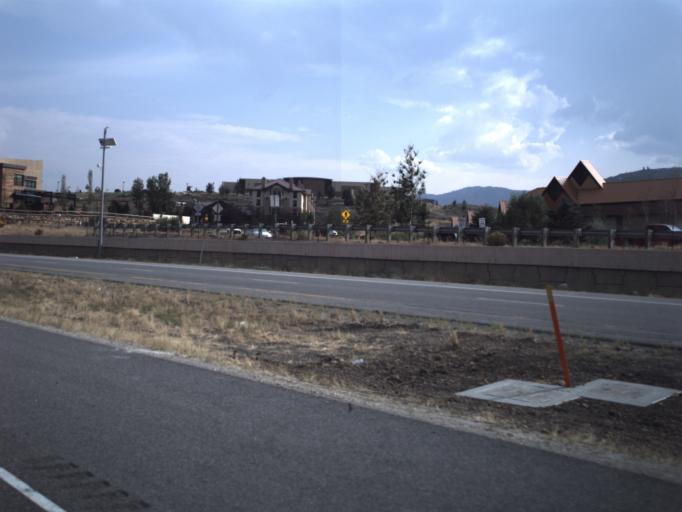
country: US
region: Utah
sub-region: Summit County
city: Snyderville
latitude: 40.7305
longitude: -111.5496
